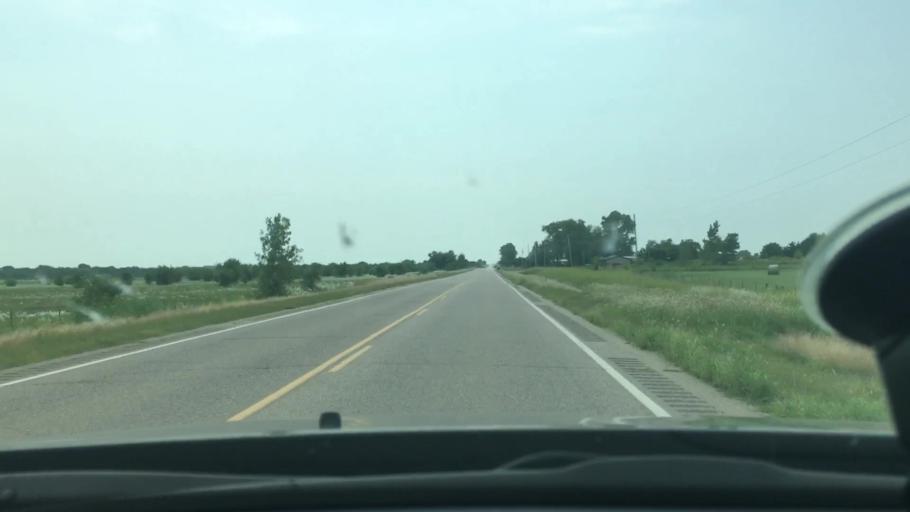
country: US
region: Oklahoma
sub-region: Marshall County
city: Madill
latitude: 34.0516
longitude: -96.7611
